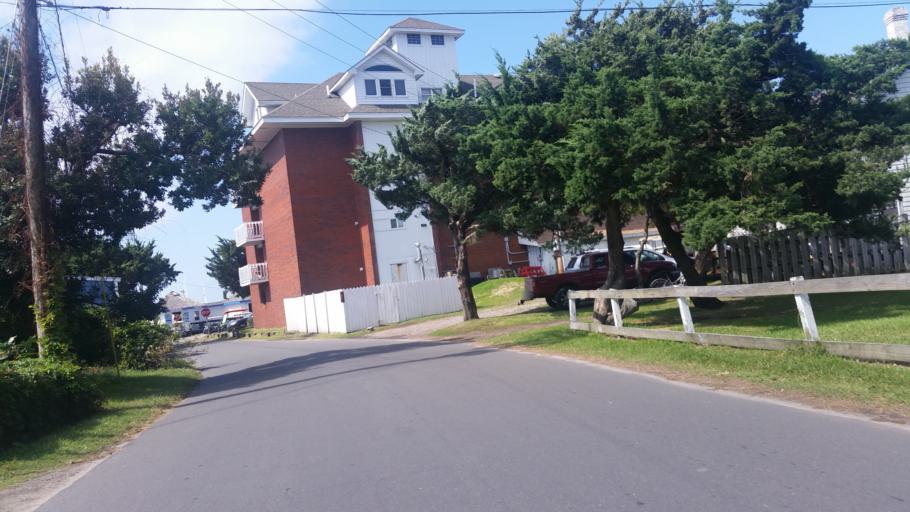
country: US
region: North Carolina
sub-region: Hyde County
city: Swanquarter
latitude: 35.1151
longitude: -75.9832
